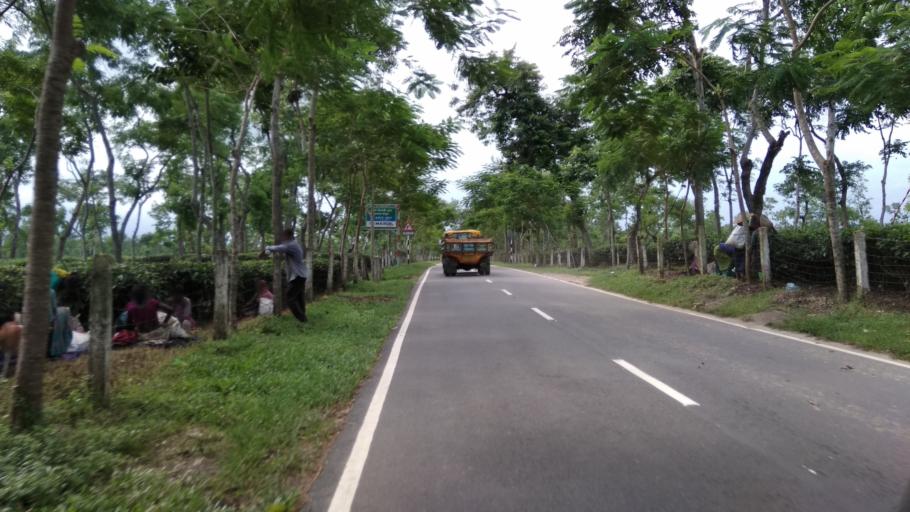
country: IN
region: Tripura
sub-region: Dhalai
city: Kamalpur
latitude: 24.3022
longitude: 91.7445
